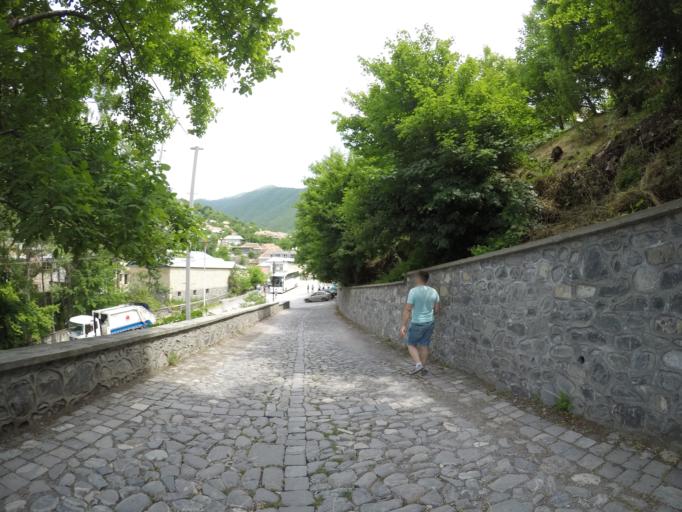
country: AZ
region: Shaki City
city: Sheki
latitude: 41.2475
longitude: 47.1891
